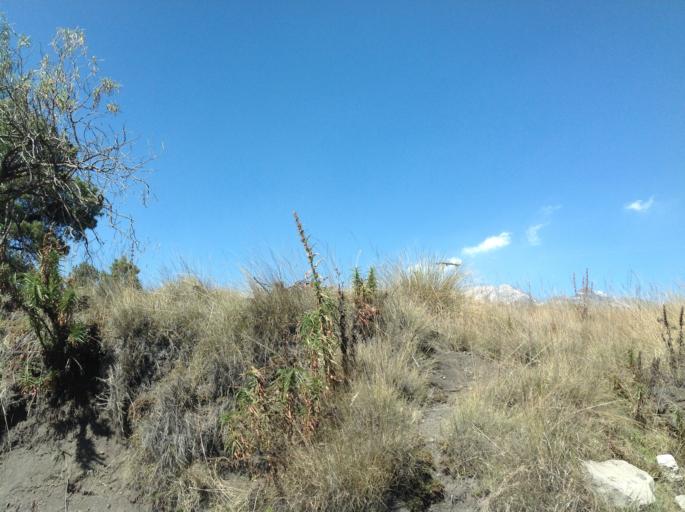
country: MX
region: Mexico
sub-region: Amecameca
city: San Diego Huehuecalco
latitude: 19.0940
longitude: -98.6507
